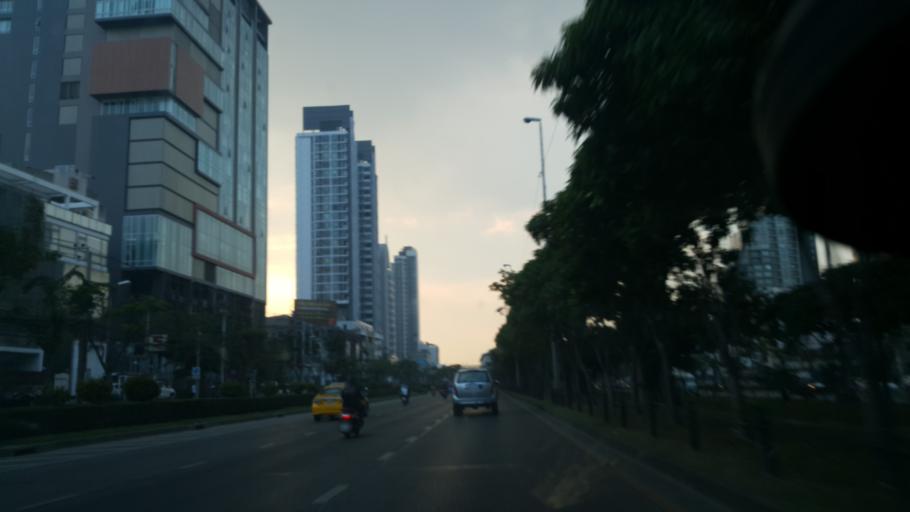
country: TH
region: Bangkok
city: Khlong San
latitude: 13.7209
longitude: 100.5000
